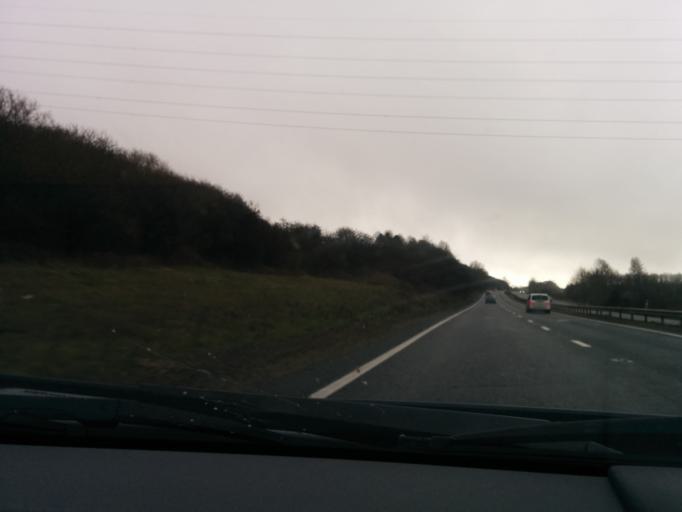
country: GB
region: England
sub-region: Hampshire
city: Highclere
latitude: 51.2951
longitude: -1.3373
